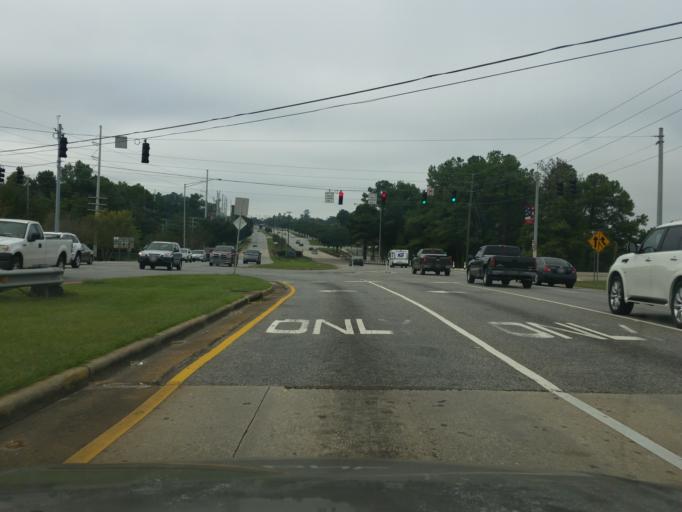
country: US
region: Alabama
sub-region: Baldwin County
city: Spanish Fort
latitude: 30.6552
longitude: -87.9120
